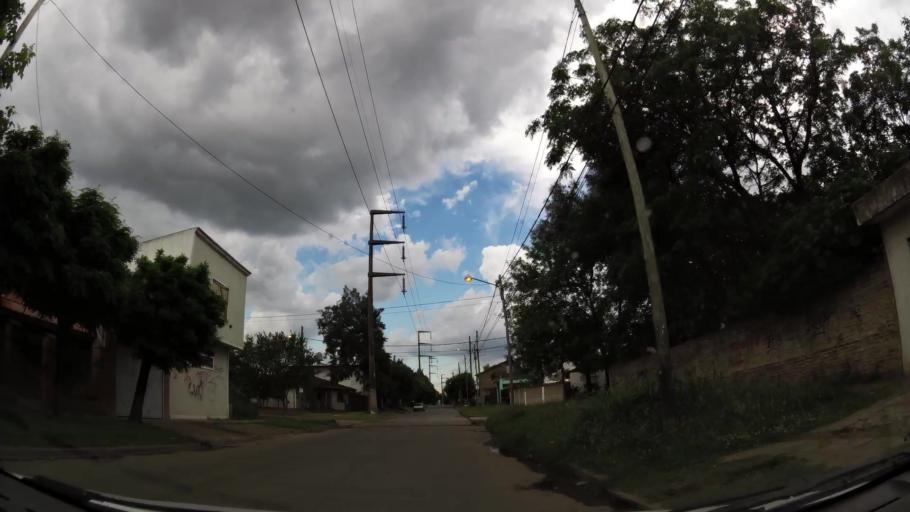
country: AR
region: Buenos Aires
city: Ituzaingo
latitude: -34.6380
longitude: -58.6823
